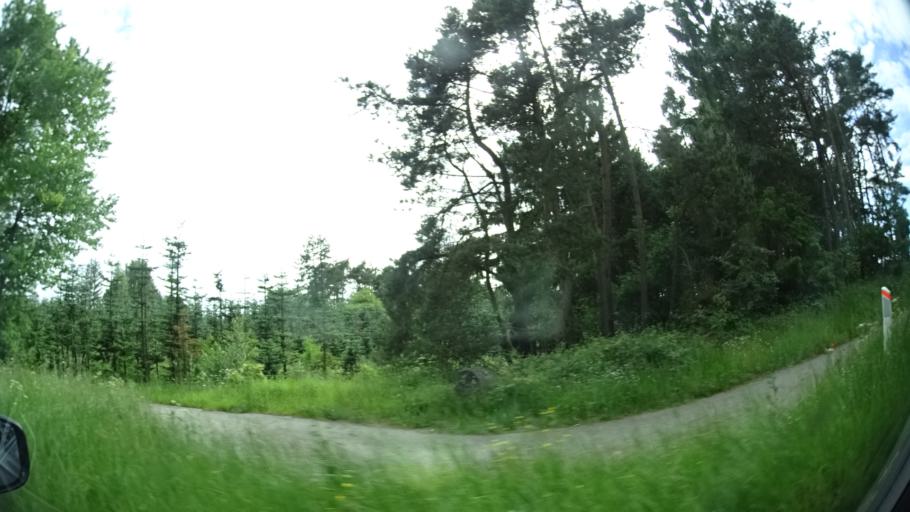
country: DK
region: Central Jutland
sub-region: Norddjurs Kommune
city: Grenaa
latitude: 56.5042
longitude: 10.7356
